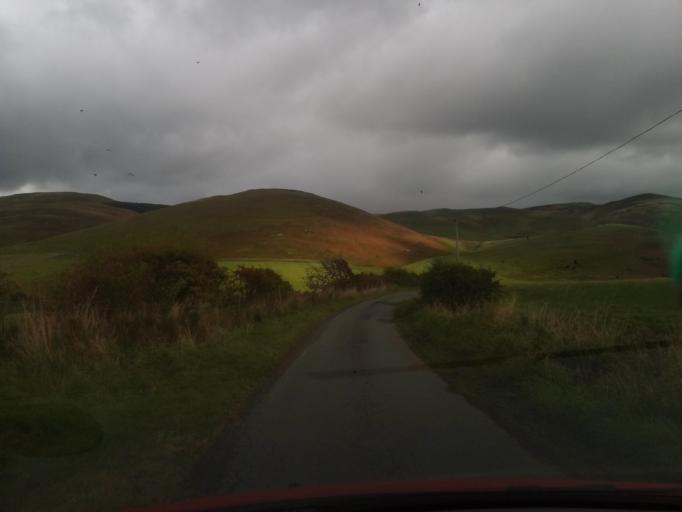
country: GB
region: Scotland
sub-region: The Scottish Borders
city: Coldstream
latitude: 55.5428
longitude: -2.2567
